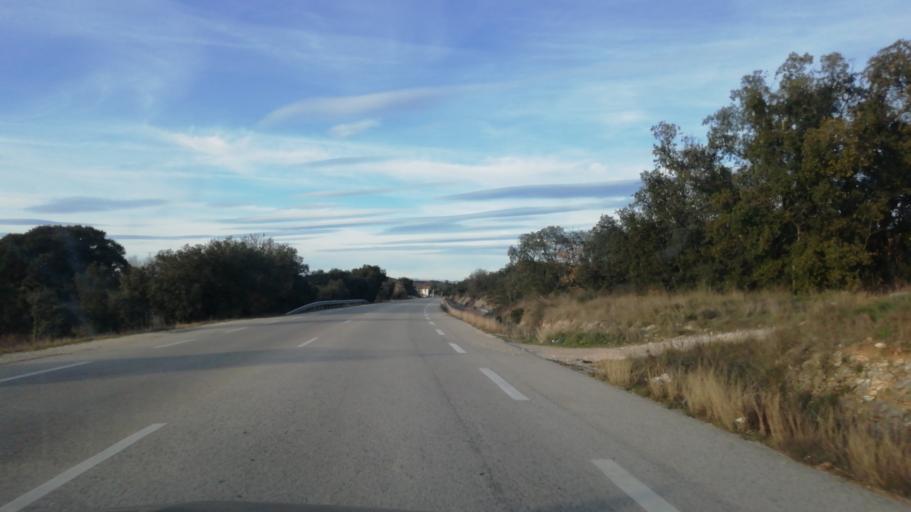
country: FR
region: Languedoc-Roussillon
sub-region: Departement du Gard
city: Quissac
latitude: 43.8981
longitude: 4.0073
